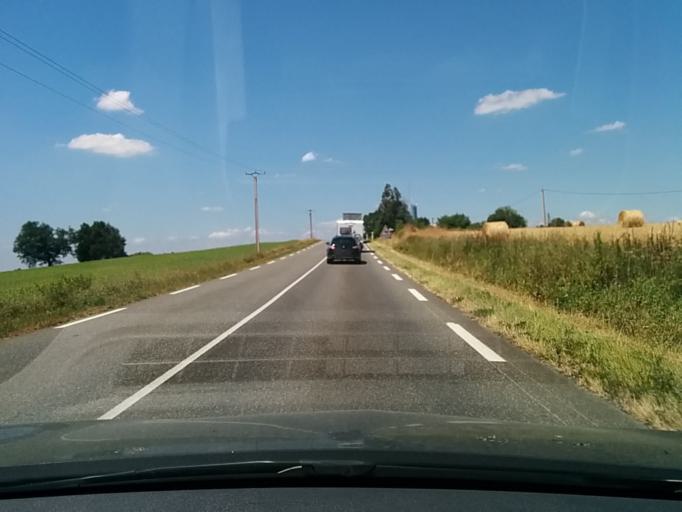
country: FR
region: Midi-Pyrenees
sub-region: Departement du Gers
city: Eauze
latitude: 43.7759
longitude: 0.1233
